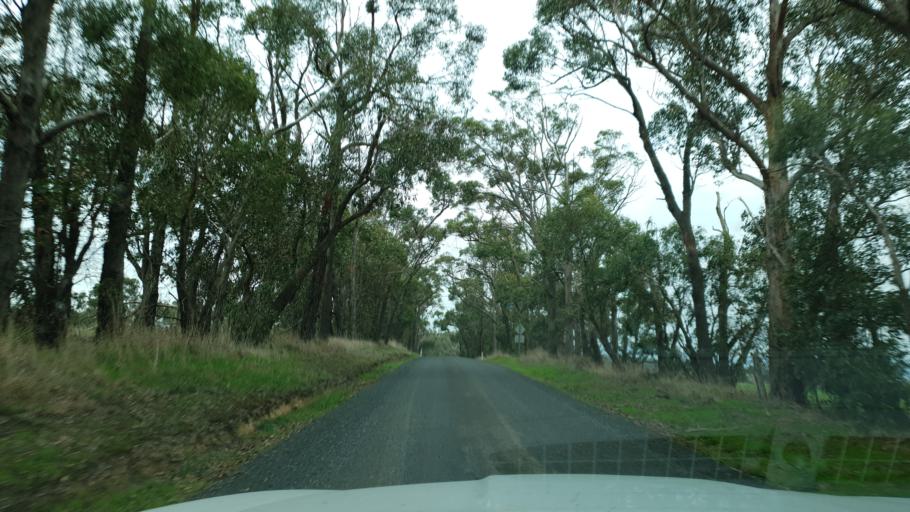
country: AU
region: Victoria
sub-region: Latrobe
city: Moe
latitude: -38.1367
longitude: 146.1132
